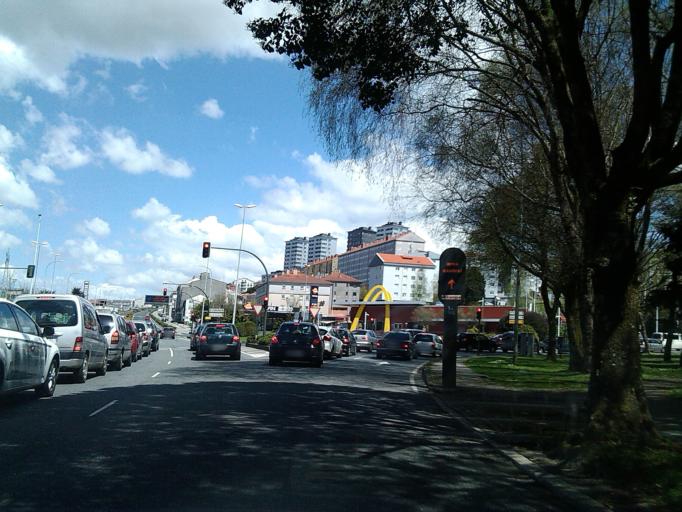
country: ES
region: Galicia
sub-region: Provincia da Coruna
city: Santiago de Compostela
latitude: 42.8910
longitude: -8.5340
